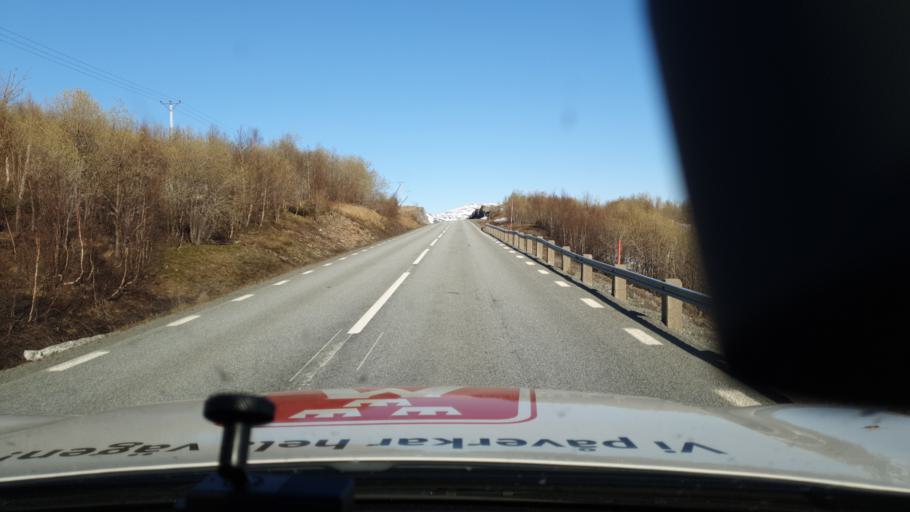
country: NO
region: Nordland
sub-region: Rana
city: Mo i Rana
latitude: 66.1231
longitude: 14.6806
